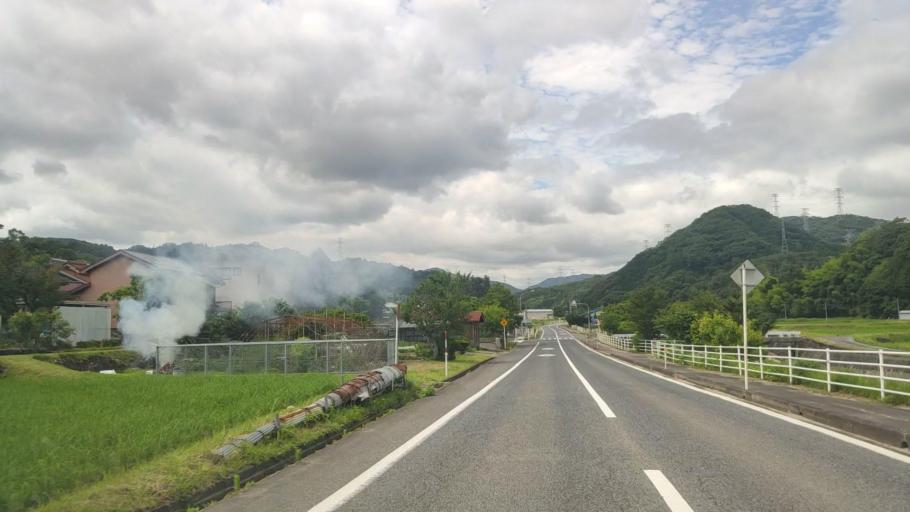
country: JP
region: Tottori
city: Yonago
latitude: 35.3023
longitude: 133.4164
